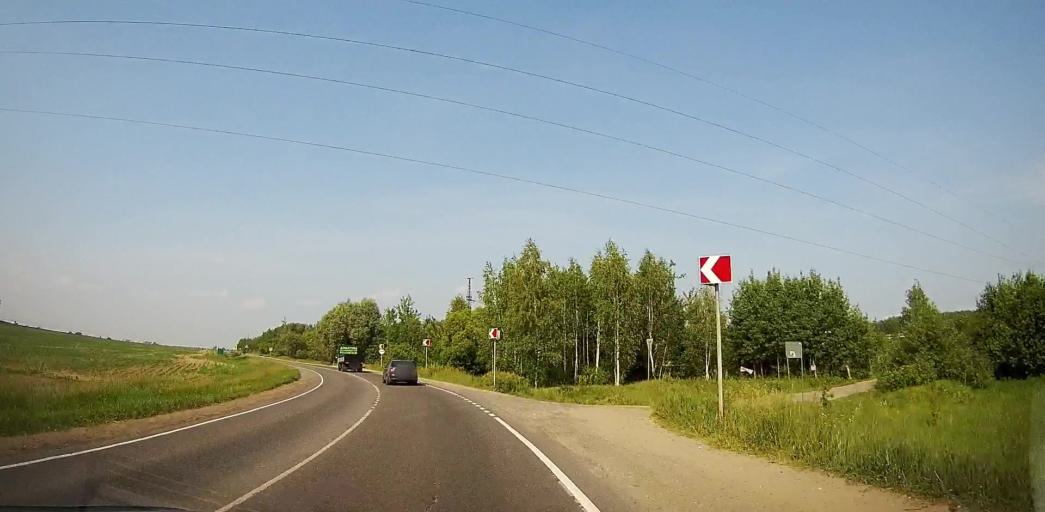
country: RU
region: Moskovskaya
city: Zhitnevo
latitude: 55.3266
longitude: 37.9014
